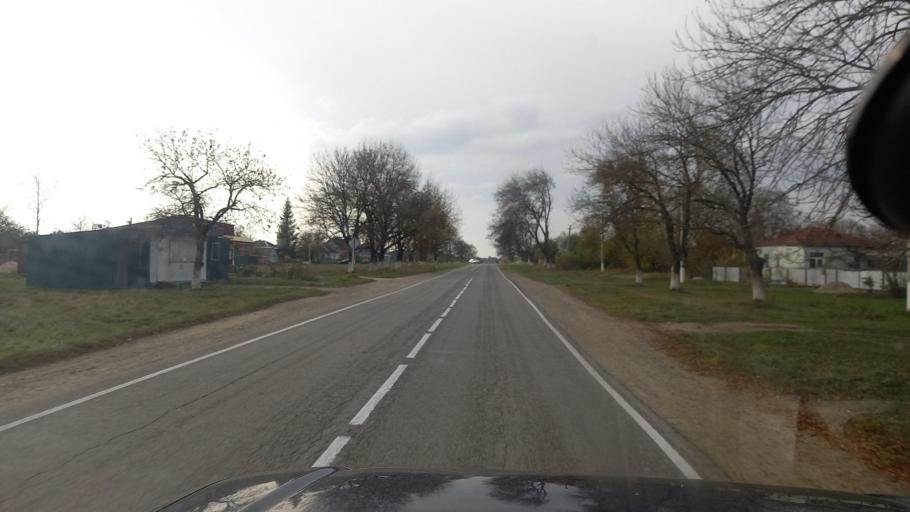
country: RU
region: Krasnodarskiy
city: Gubskaya
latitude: 44.3188
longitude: 40.6151
